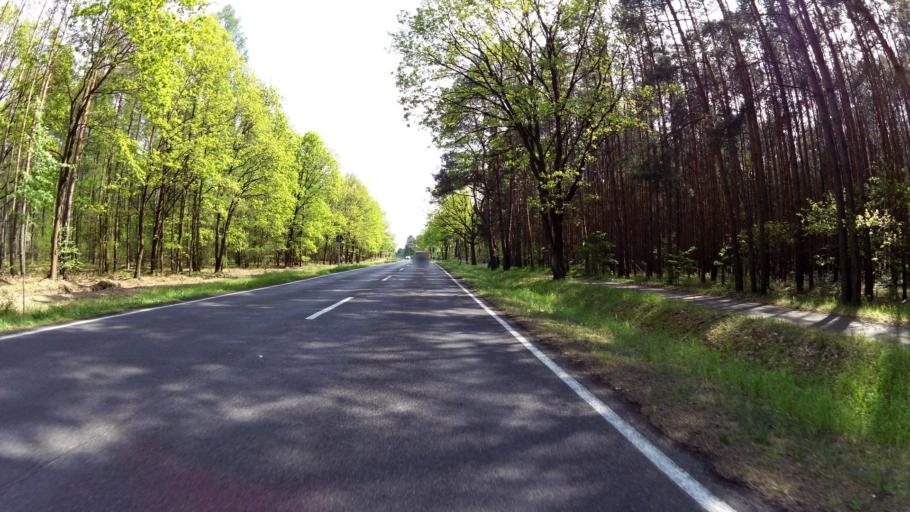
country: DE
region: Brandenburg
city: Spreenhagen
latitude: 52.3683
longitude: 13.8379
